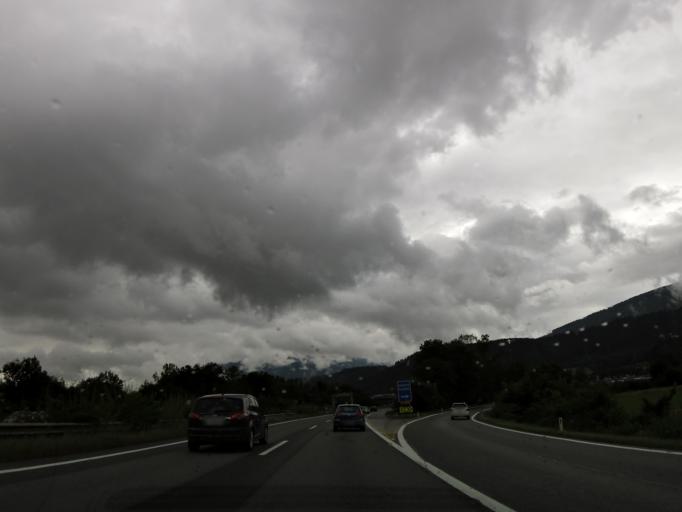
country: AT
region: Tyrol
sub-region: Politischer Bezirk Innsbruck Land
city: Vols
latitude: 47.2628
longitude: 11.3193
